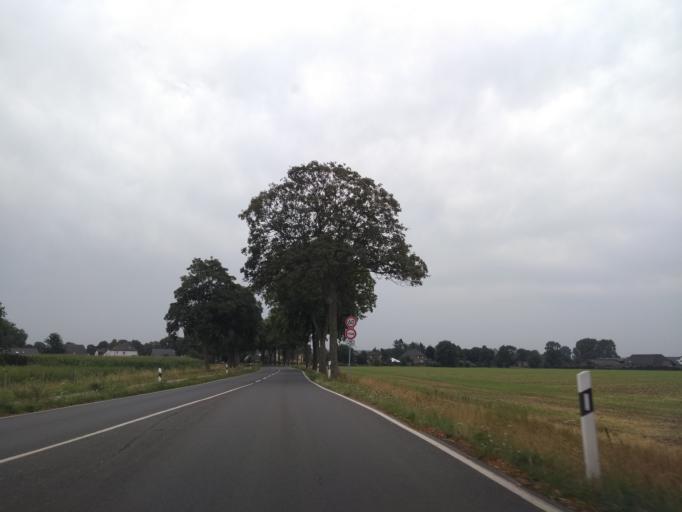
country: DE
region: North Rhine-Westphalia
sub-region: Regierungsbezirk Dusseldorf
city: Kleve
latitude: 51.8300
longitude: 6.1012
